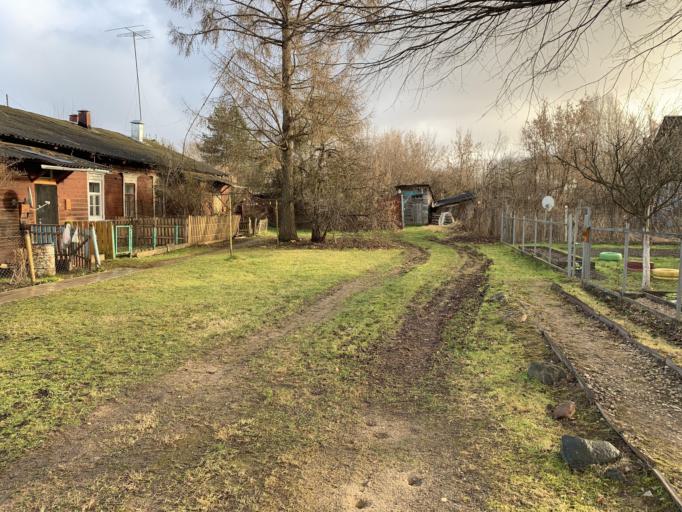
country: RU
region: Tverskaya
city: Likhoslavl'
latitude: 57.1270
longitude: 35.4646
